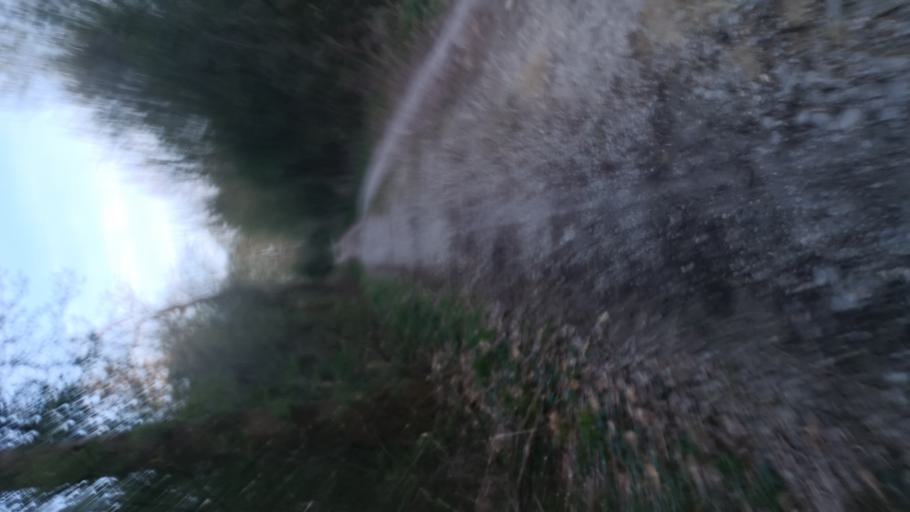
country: DE
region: Bavaria
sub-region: Upper Bavaria
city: Planegg
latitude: 48.0685
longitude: 11.4130
